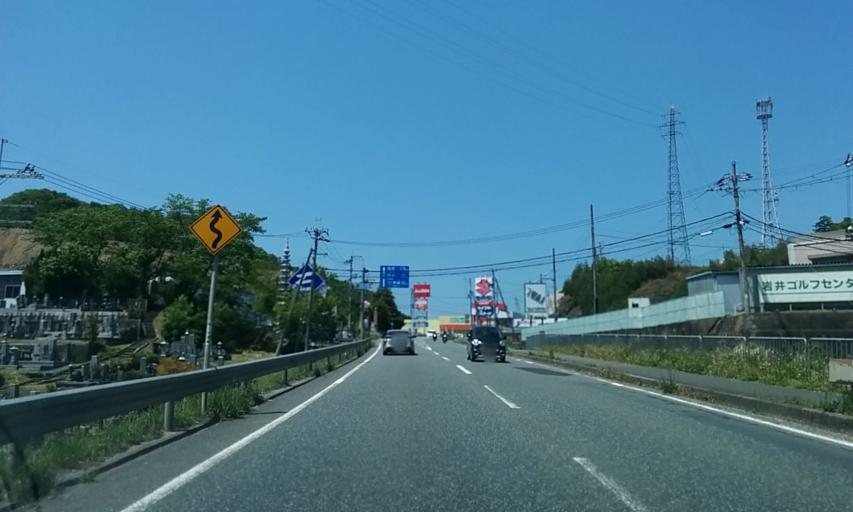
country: JP
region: Kyoto
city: Fukuchiyama
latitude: 35.3135
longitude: 135.1019
